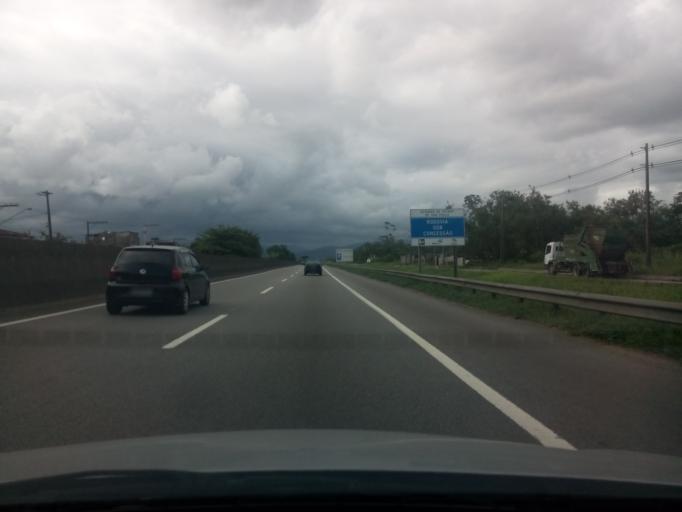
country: BR
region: Sao Paulo
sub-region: Guaruja
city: Guaruja
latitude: -23.9578
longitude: -46.2745
